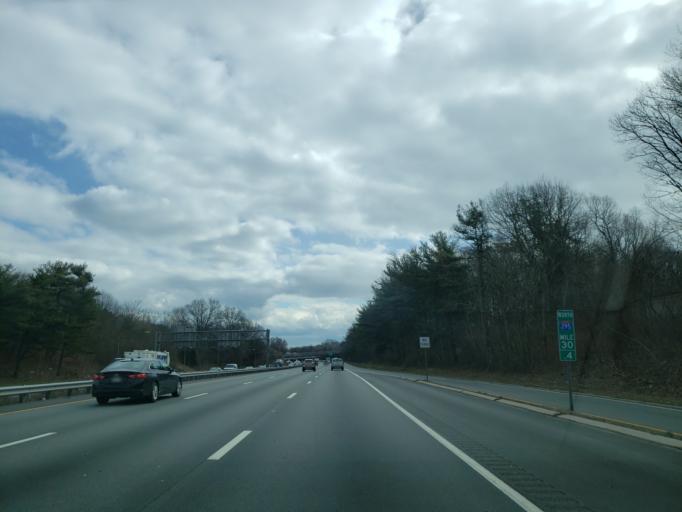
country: US
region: New Jersey
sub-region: Camden County
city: Lawnside
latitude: 39.8747
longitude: -75.0421
